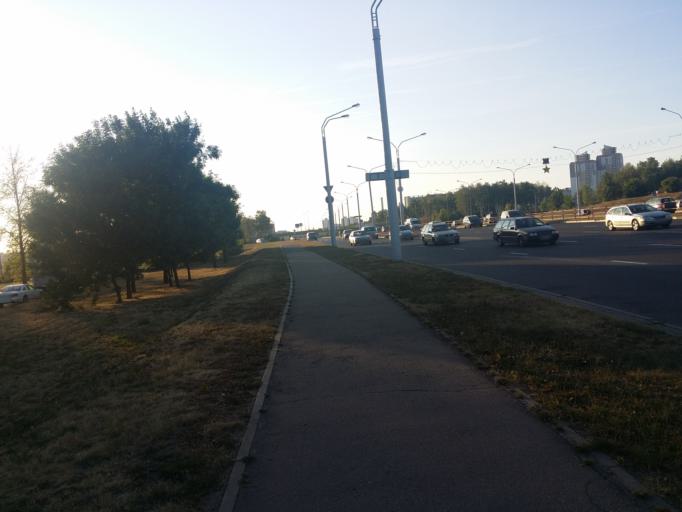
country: BY
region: Minsk
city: Vyaliki Trastsyanets
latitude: 53.8569
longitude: 27.6868
